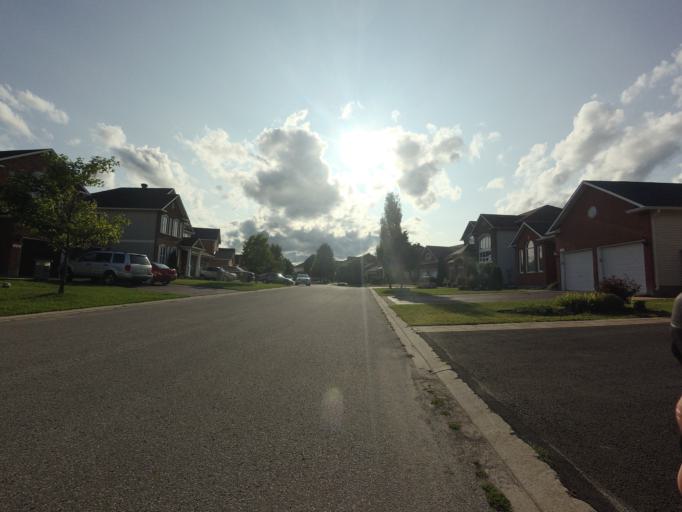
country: CA
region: Ontario
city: Bells Corners
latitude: 45.2912
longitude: -75.7121
